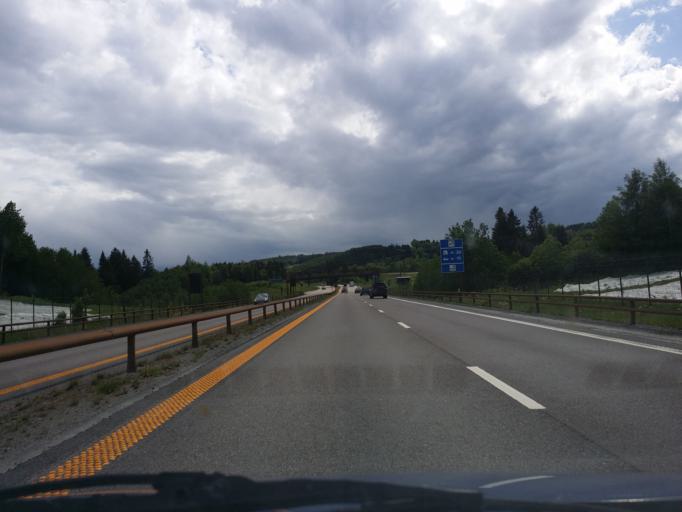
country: NO
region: Akershus
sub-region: Eidsvoll
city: Eidsvoll
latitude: 60.3733
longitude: 11.2057
